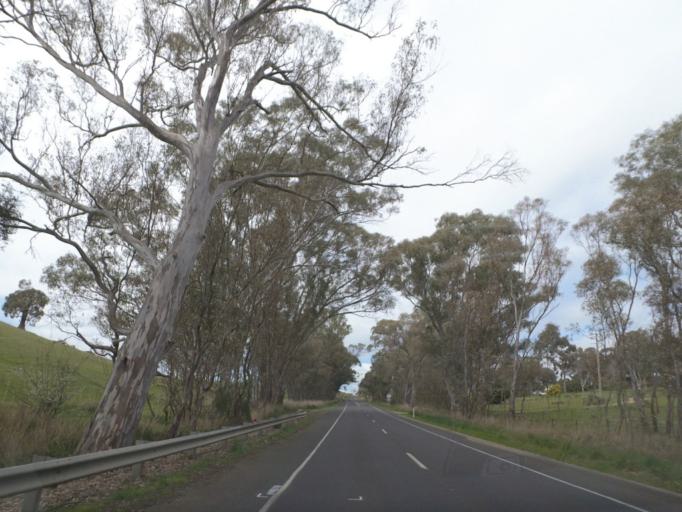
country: AU
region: Victoria
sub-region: Murrindindi
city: Kinglake West
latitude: -37.1541
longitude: 145.2797
